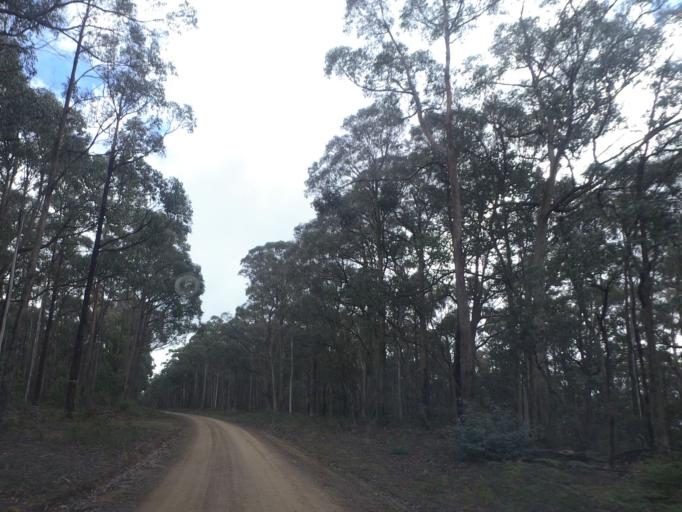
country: AU
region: Victoria
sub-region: Moorabool
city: Bacchus Marsh
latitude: -37.4394
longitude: 144.3219
